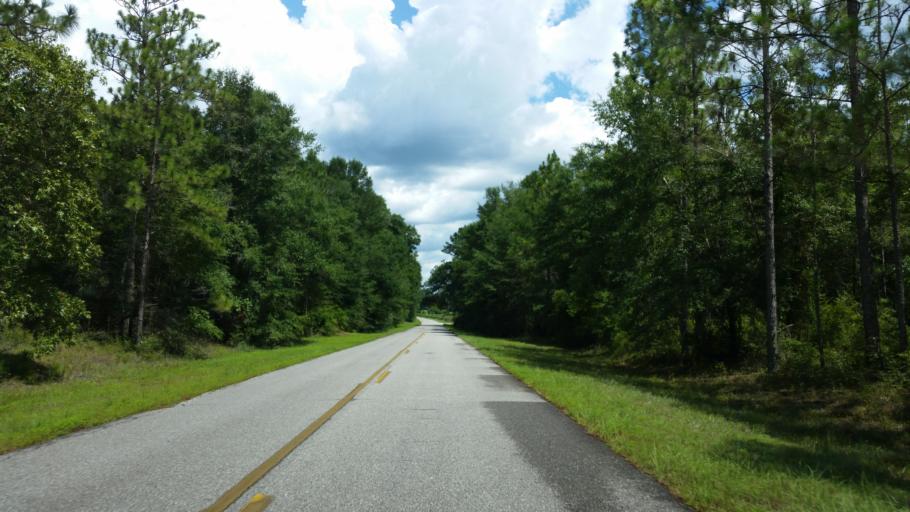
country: US
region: Florida
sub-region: Santa Rosa County
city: East Milton
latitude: 30.7372
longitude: -86.8182
